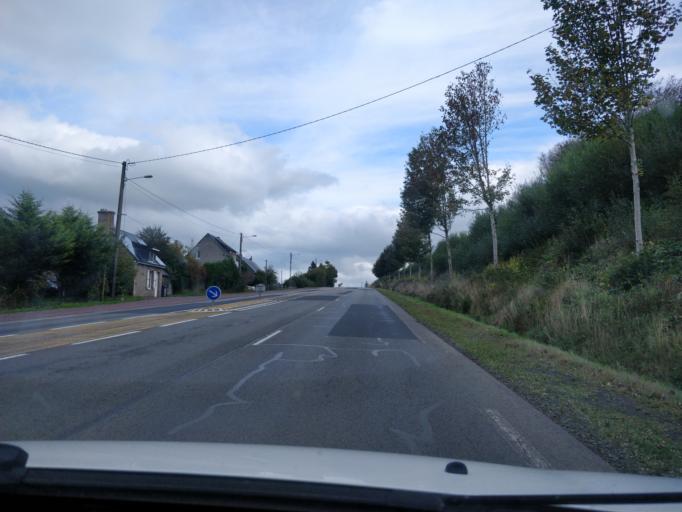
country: FR
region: Lower Normandy
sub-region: Departement du Calvados
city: Saint-Sever-Calvados
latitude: 48.8384
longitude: -1.0362
